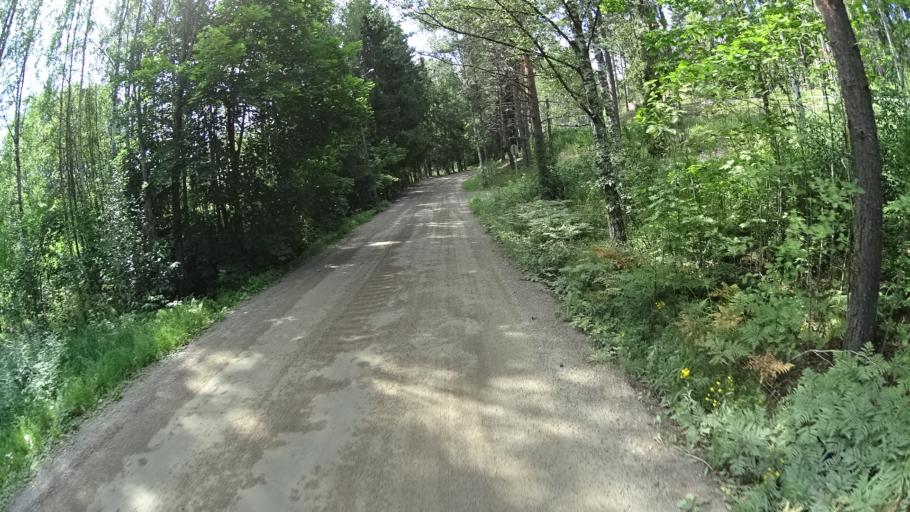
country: FI
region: Uusimaa
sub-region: Porvoo
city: Porvoo
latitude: 60.3942
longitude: 25.7120
